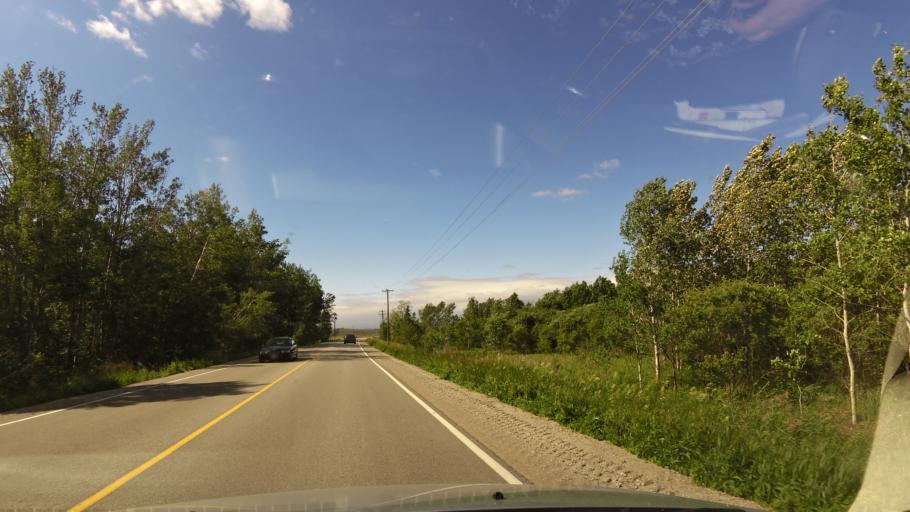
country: CA
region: Ontario
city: Innisfil
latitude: 44.2110
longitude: -79.6288
